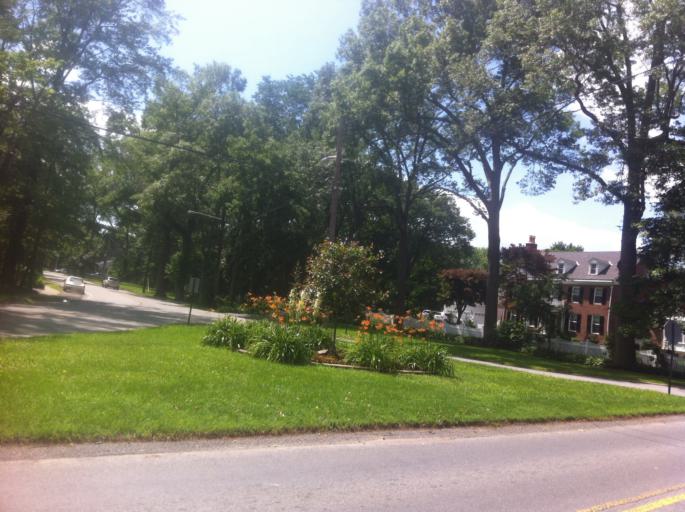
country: US
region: New York
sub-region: Nassau County
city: Glen Cove
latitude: 40.8664
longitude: -73.6172
